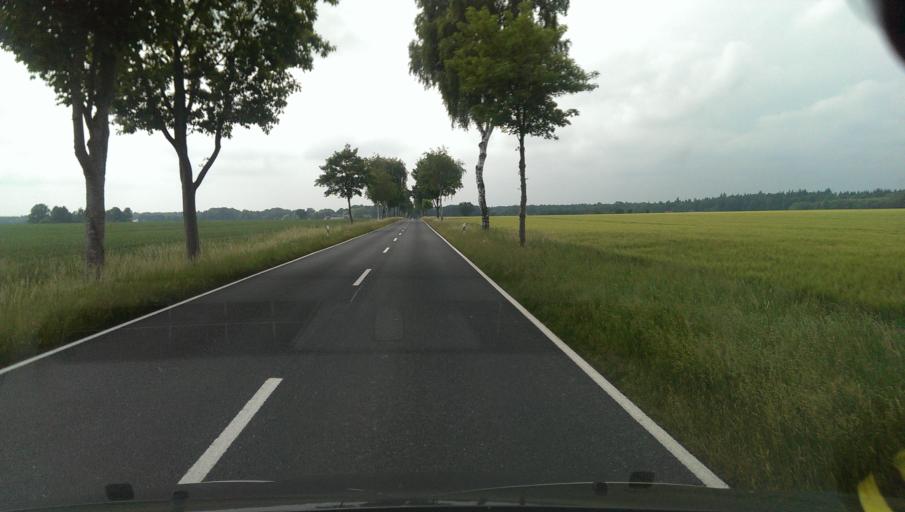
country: DE
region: Lower Saxony
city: Sprakensehl
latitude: 52.7675
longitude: 10.4729
